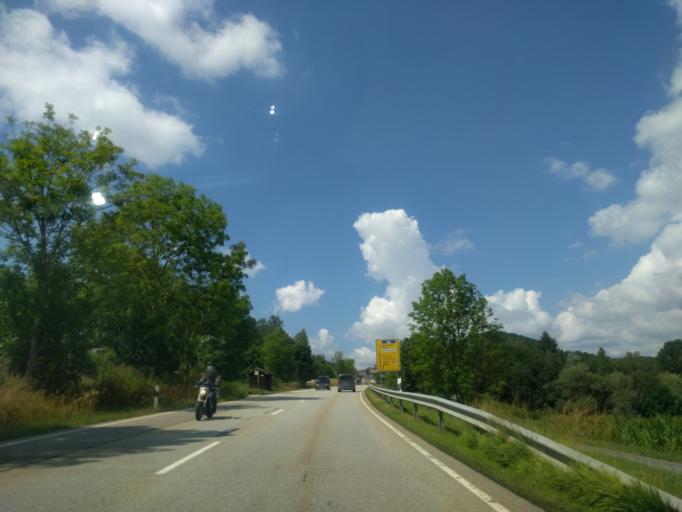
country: DE
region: Bavaria
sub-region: Lower Bavaria
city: Grafenau
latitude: 48.8293
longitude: 13.3496
